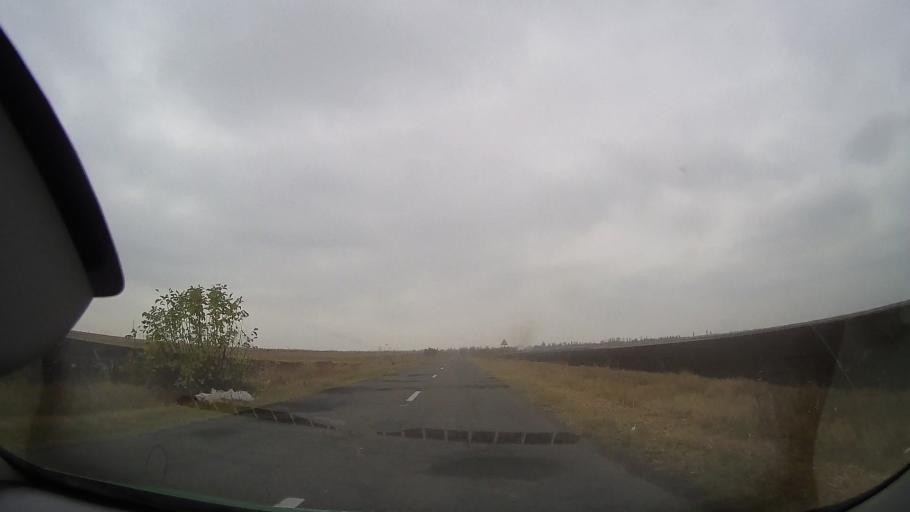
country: RO
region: Ialomita
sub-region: Comuna Valea Macrisului
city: Valea Macrisului
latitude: 44.7605
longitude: 26.8001
